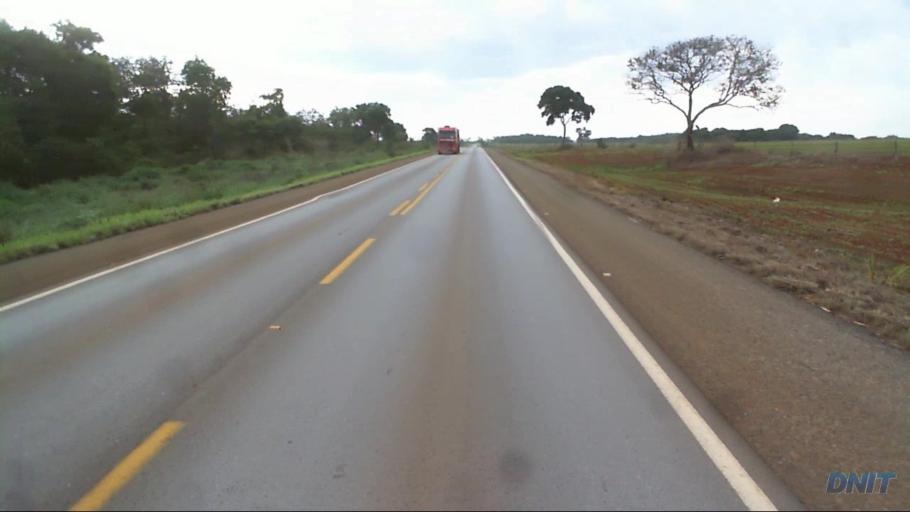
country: BR
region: Goias
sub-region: Uruacu
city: Uruacu
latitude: -14.6694
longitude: -49.1464
